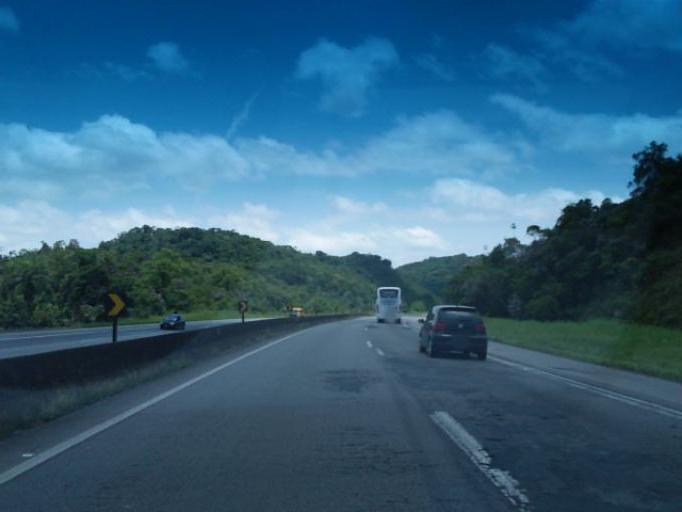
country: BR
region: Sao Paulo
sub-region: Juquia
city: Juquia
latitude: -24.3759
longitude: -47.7084
